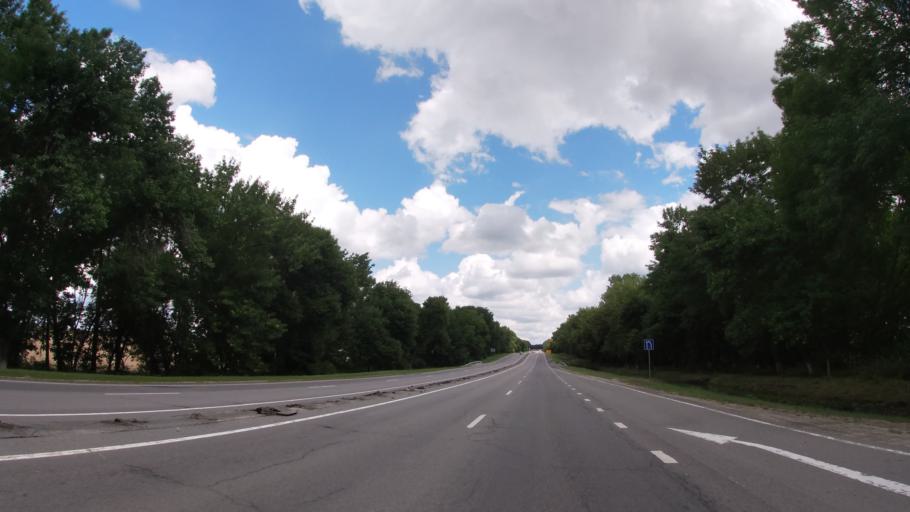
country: RU
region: Belgorod
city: Mayskiy
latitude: 50.4389
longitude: 36.3924
